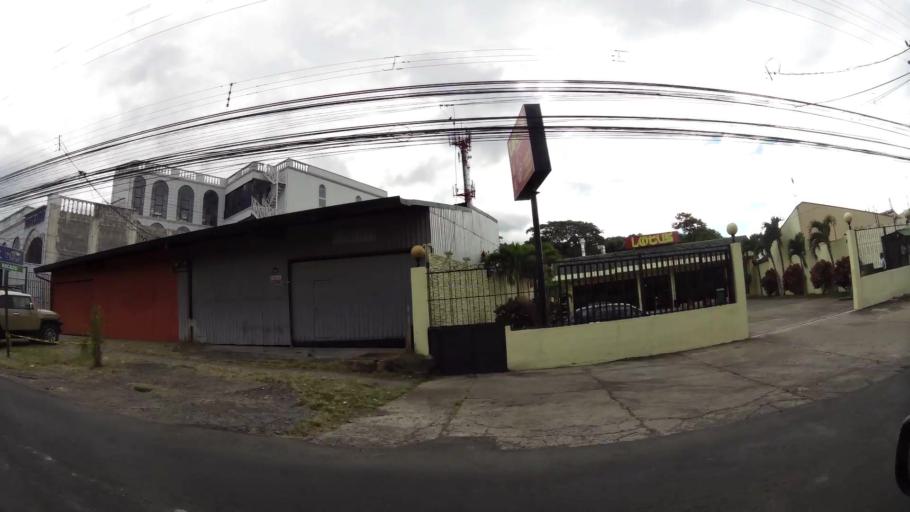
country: CR
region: San Jose
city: San Rafael
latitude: 9.9312
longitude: -84.1512
